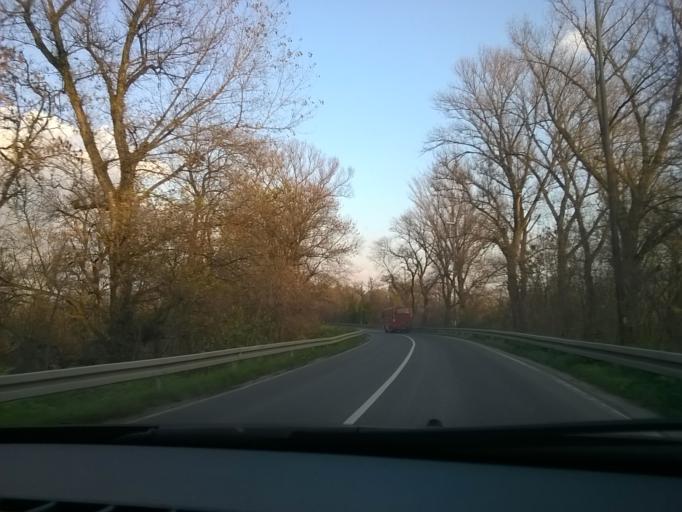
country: RS
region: Autonomna Pokrajina Vojvodina
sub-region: Juznobanatski Okrug
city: Pancevo
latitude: 44.8684
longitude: 20.6260
